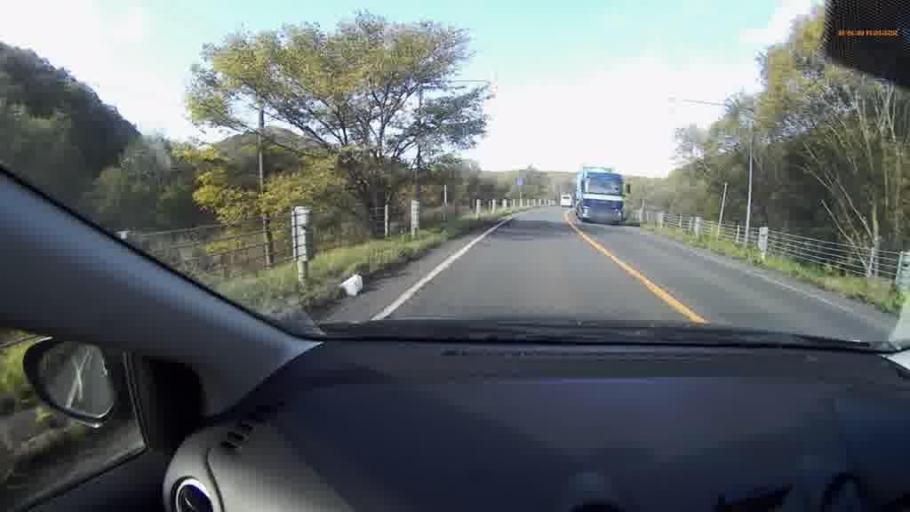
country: JP
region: Hokkaido
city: Kushiro
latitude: 42.9965
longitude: 144.4840
